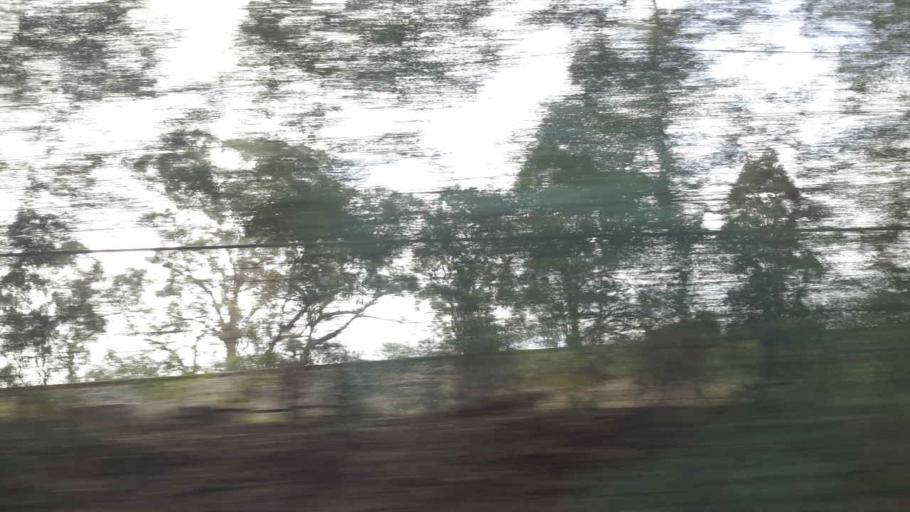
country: AU
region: New South Wales
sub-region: Campbelltown Municipality
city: Glen Alpine
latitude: -34.0778
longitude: 150.7842
